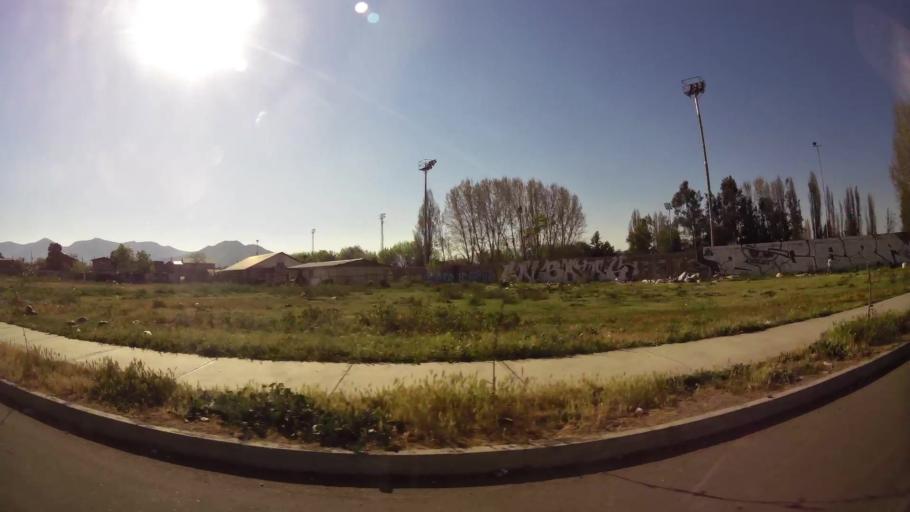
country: CL
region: Santiago Metropolitan
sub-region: Provincia de Talagante
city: Penaflor
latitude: -33.6071
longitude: -70.8724
